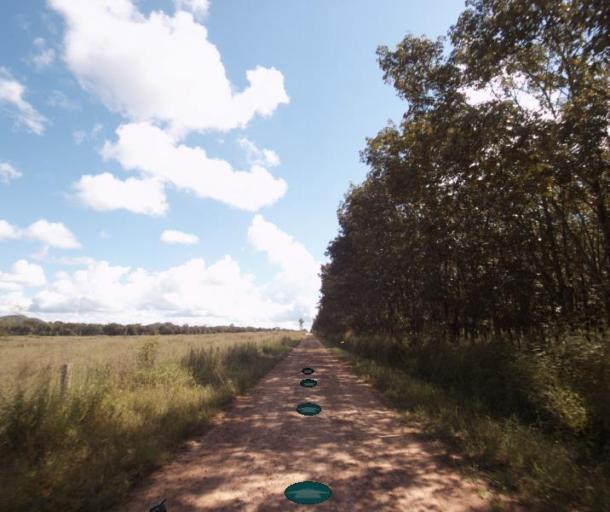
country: BR
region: Goias
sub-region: Pirenopolis
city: Pirenopolis
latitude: -15.7788
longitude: -49.0401
